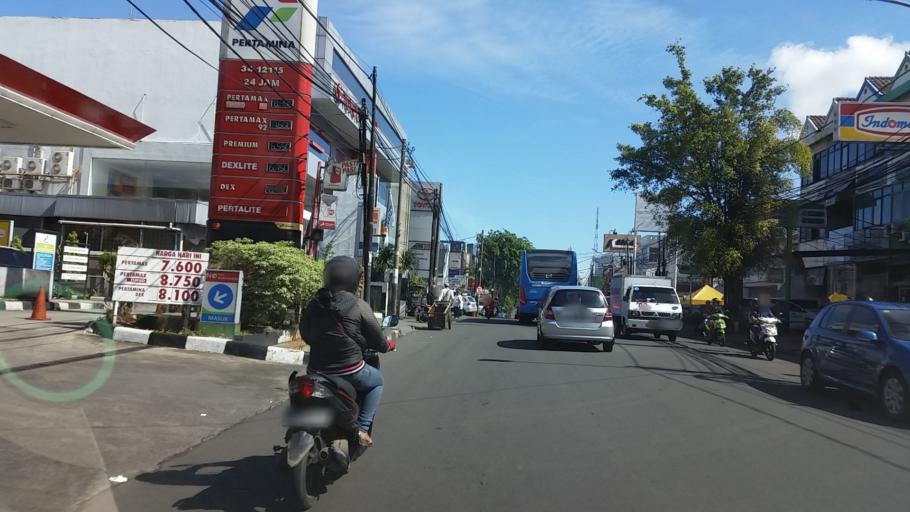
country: ID
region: Jakarta Raya
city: Jakarta
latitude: -6.2599
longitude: 106.7891
